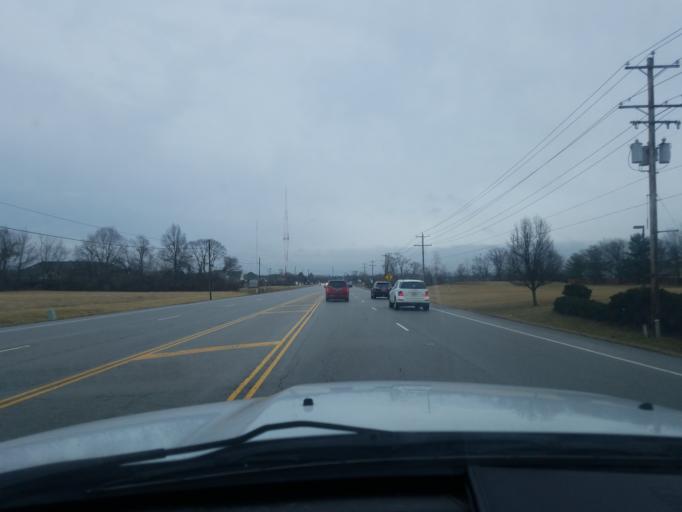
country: US
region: Ohio
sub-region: Warren County
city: Mason
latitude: 39.3519
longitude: -84.3389
